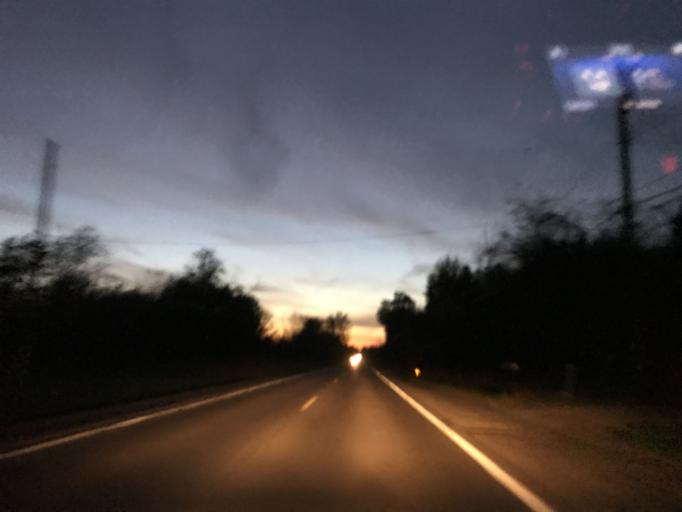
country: US
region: Michigan
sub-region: Wayne County
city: Northville
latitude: 42.4350
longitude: -83.5572
